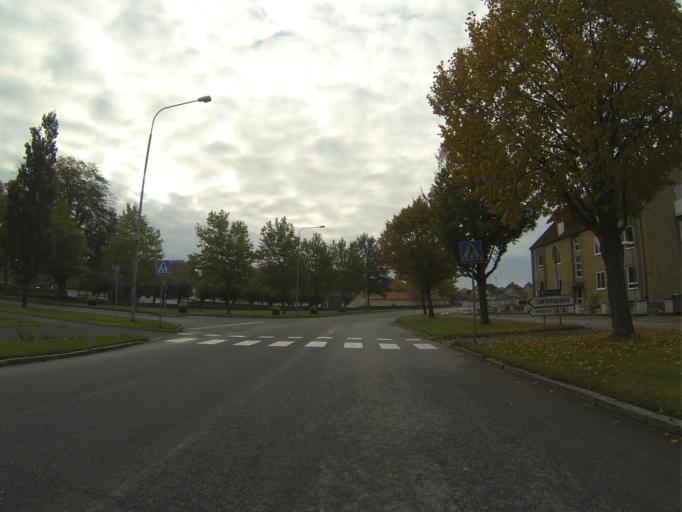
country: SE
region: Skane
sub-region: Tomelilla Kommun
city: Tomelilla
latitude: 55.5414
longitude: 13.9442
